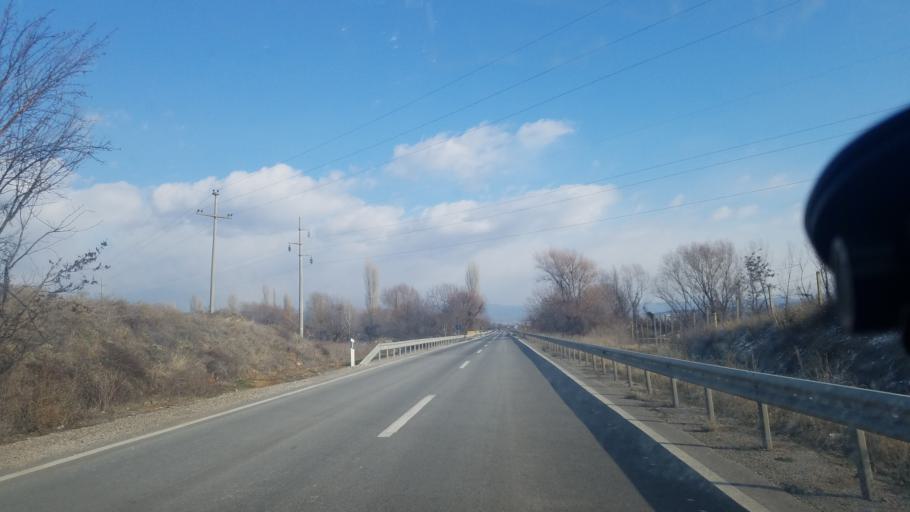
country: MK
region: Kocani
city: Kochani
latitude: 41.9021
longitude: 22.4009
